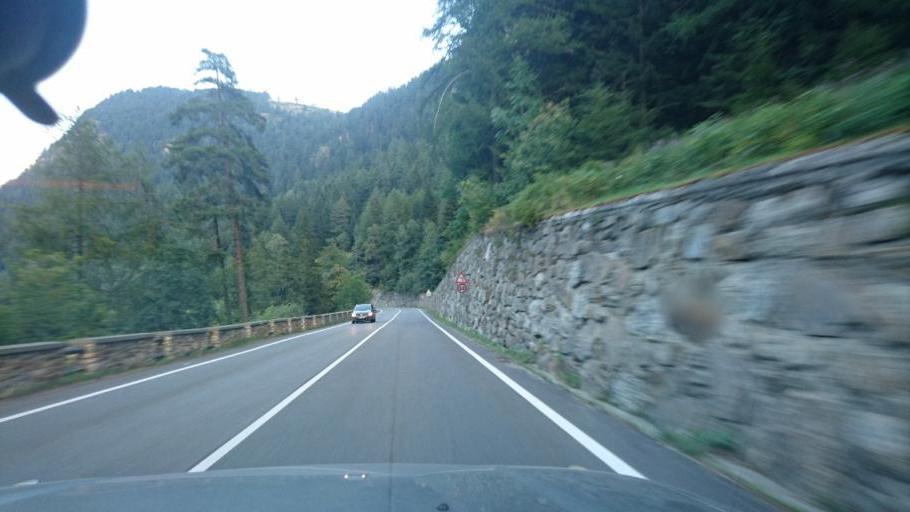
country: IT
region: Aosta Valley
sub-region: Valle d'Aosta
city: La Thuile
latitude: 45.7283
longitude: 6.9556
